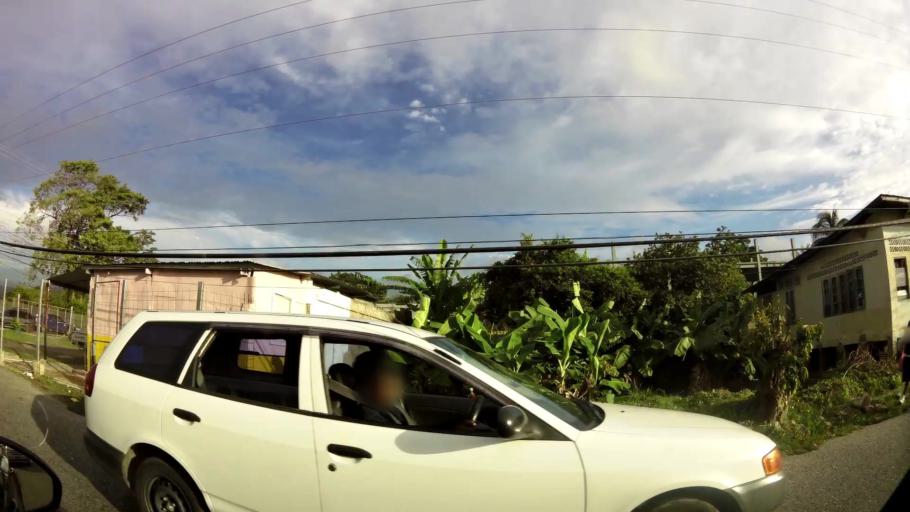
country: TT
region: Tunapuna/Piarco
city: Tunapuna
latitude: 10.6428
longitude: -61.4097
